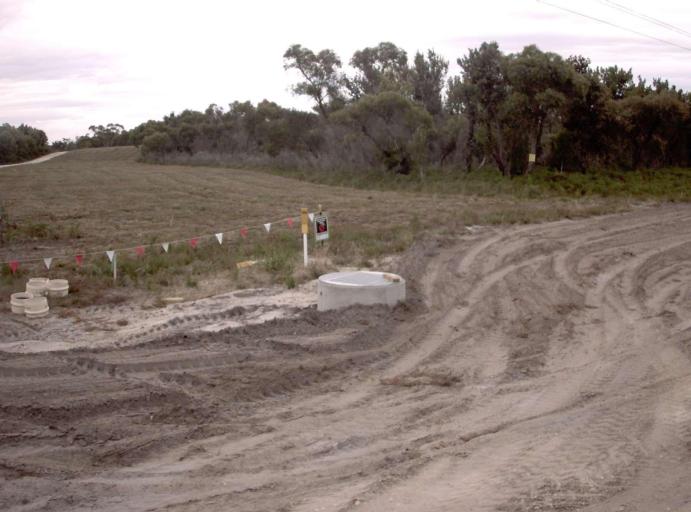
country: AU
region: Victoria
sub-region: East Gippsland
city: Bairnsdale
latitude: -38.0815
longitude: 147.5321
